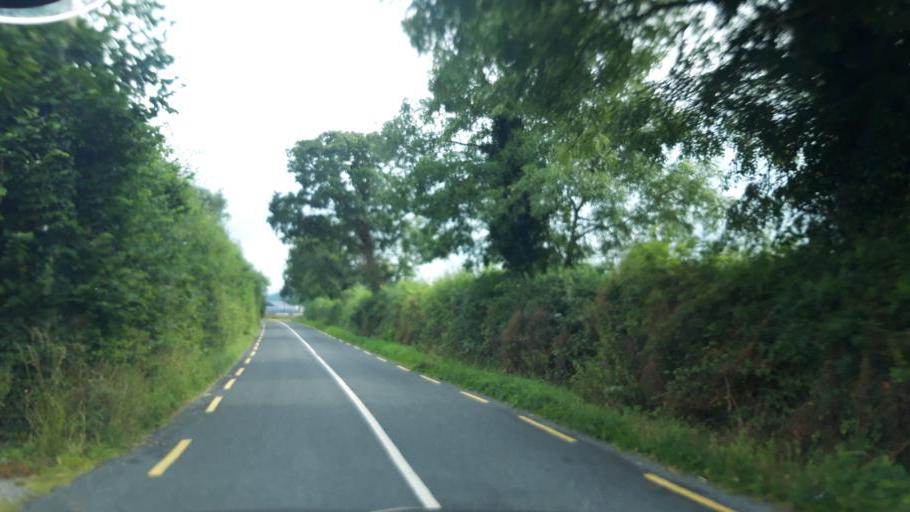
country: IE
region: Leinster
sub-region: Kilkenny
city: Ballyragget
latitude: 52.7515
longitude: -7.3917
